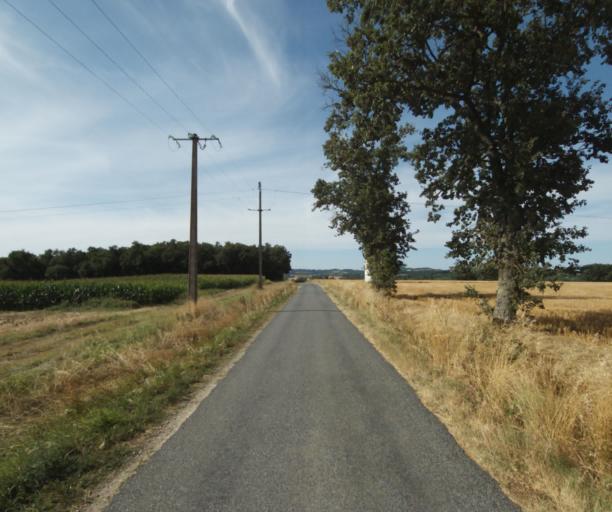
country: FR
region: Midi-Pyrenees
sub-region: Departement du Tarn
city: Soreze
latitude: 43.5043
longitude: 2.0467
